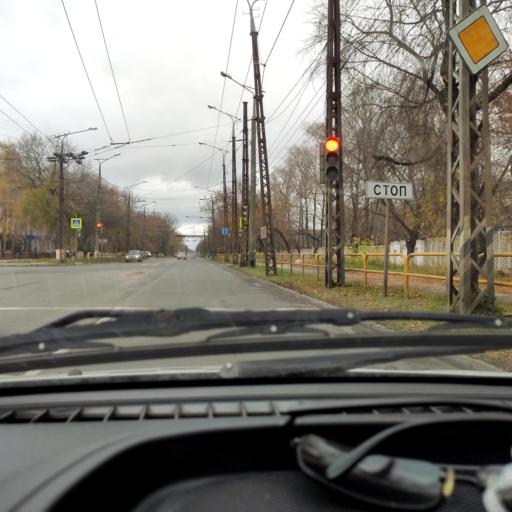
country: RU
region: Samara
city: Tol'yatti
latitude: 53.5197
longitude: 49.4321
